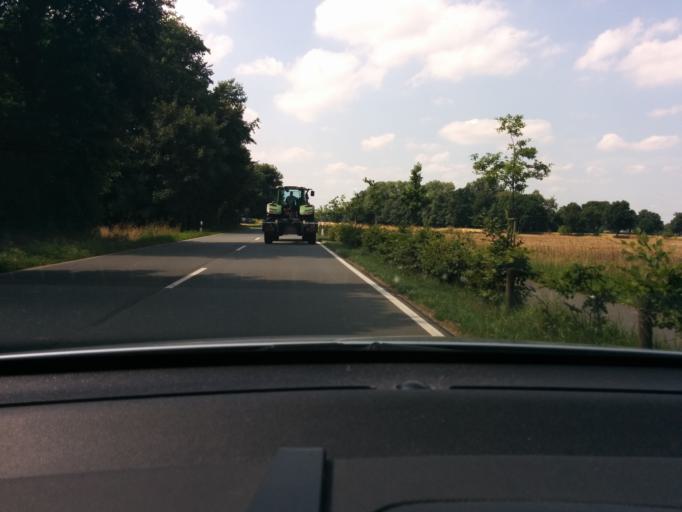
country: DE
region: North Rhine-Westphalia
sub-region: Regierungsbezirk Munster
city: Wettringen
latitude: 52.1764
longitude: 7.2814
